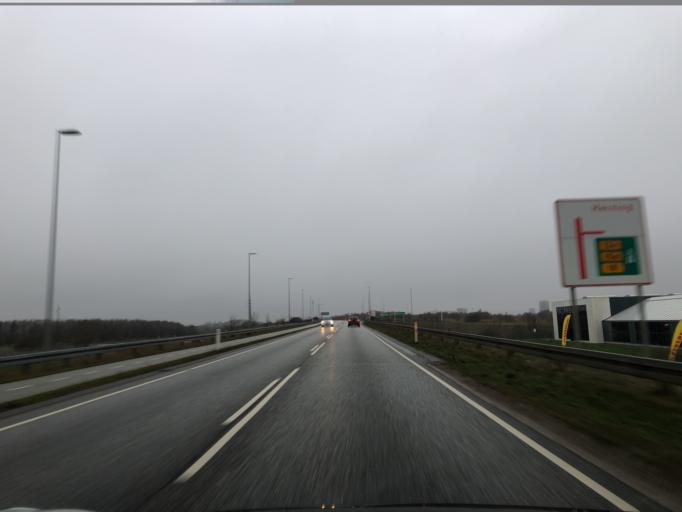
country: DK
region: Central Jutland
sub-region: Herning Kommune
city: Lind
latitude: 56.1136
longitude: 8.9763
